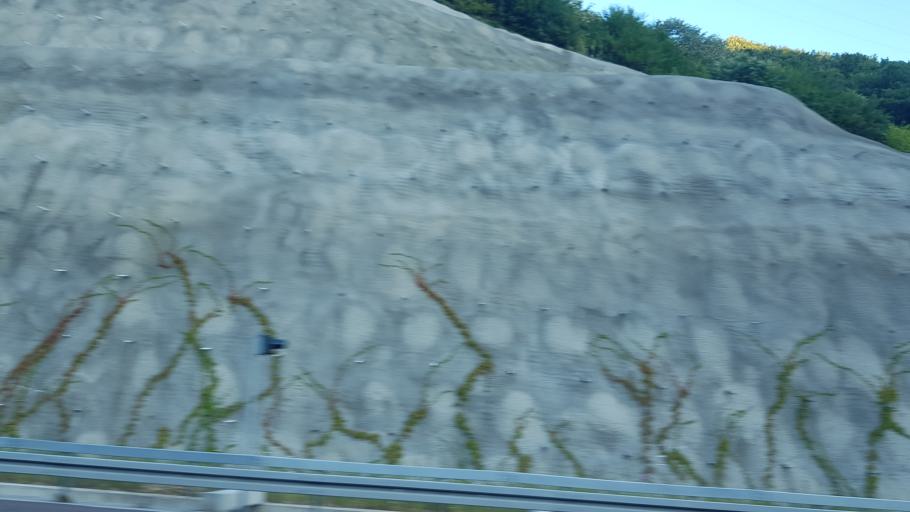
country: TR
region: Bursa
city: Yenikoy
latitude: 40.5859
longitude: 29.3636
